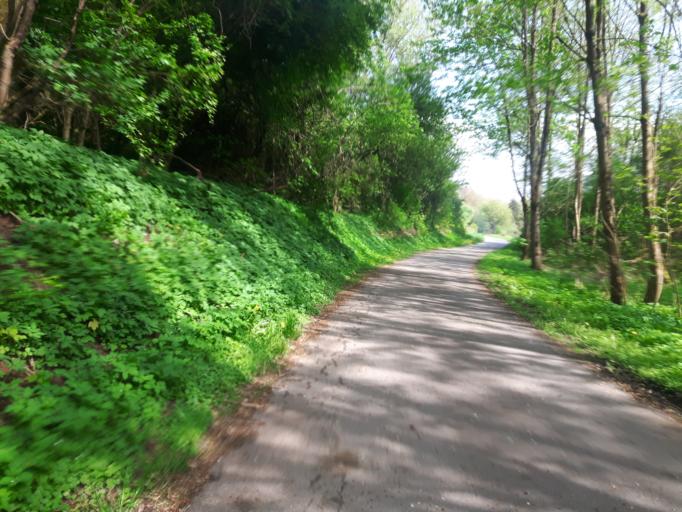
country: DE
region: Baden-Wuerttemberg
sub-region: Karlsruhe Region
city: Muhlhausen
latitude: 49.2480
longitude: 8.7465
